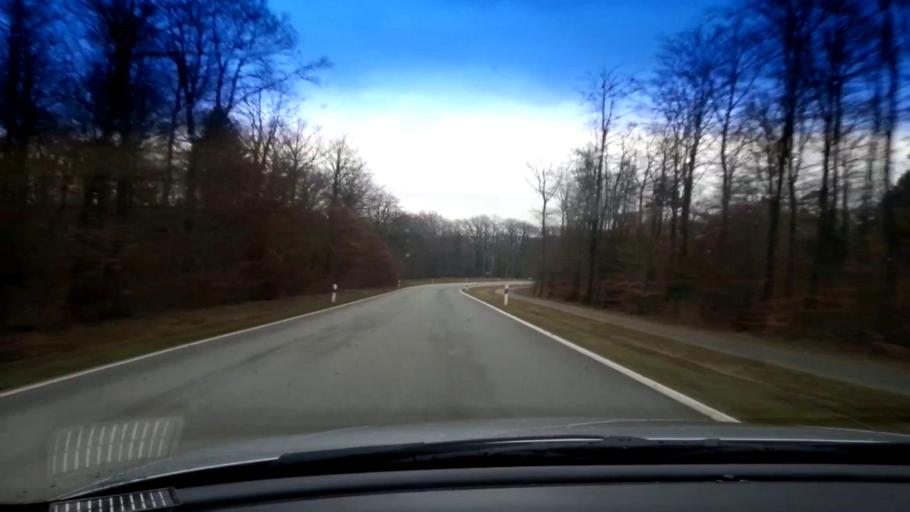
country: DE
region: Bavaria
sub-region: Upper Franconia
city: Litzendorf
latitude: 49.9302
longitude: 10.9965
